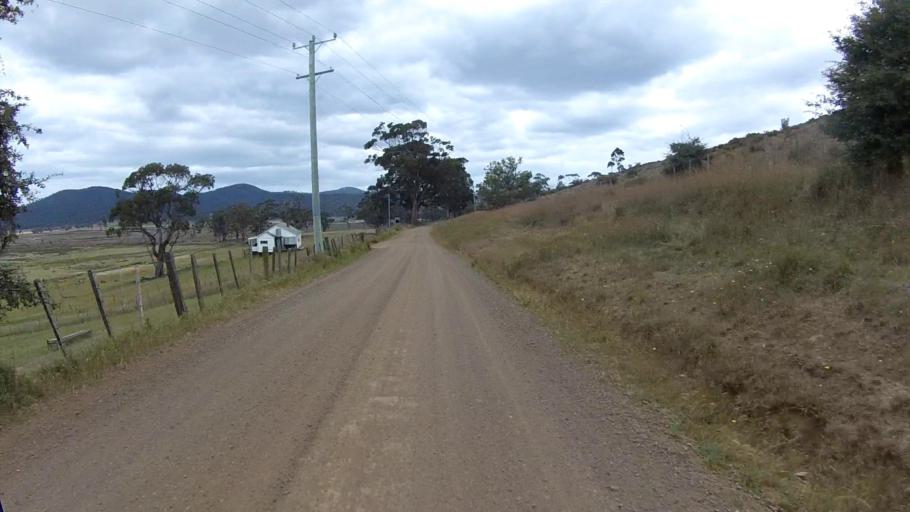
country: AU
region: Tasmania
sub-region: Sorell
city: Sorell
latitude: -42.6300
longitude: 147.9288
